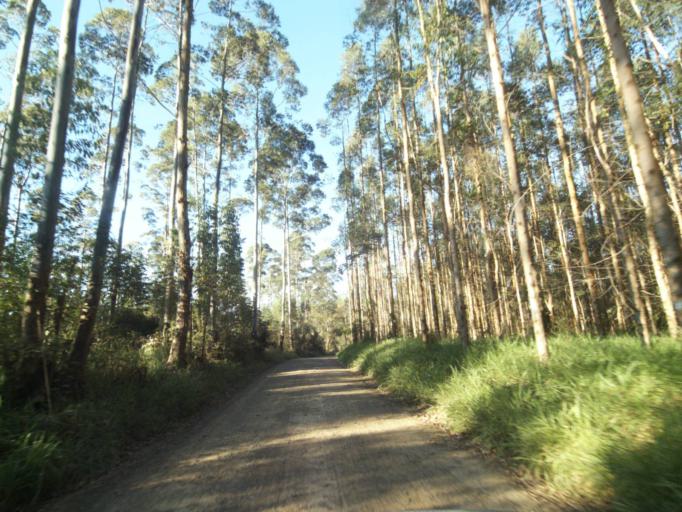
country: BR
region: Parana
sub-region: Telemaco Borba
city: Telemaco Borba
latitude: -24.4936
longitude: -50.5985
